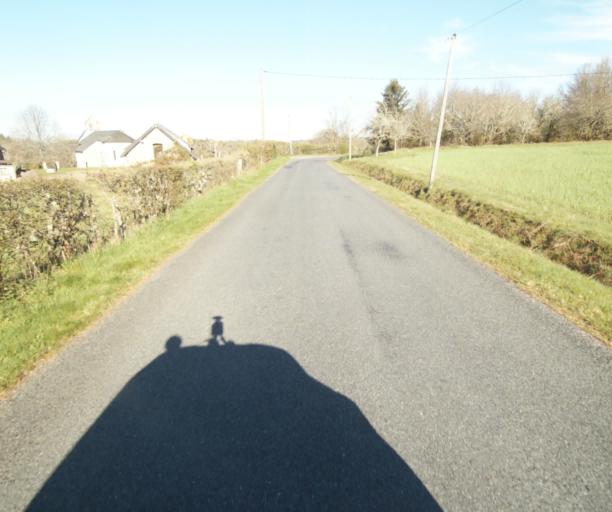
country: FR
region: Limousin
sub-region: Departement de la Correze
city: Correze
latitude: 45.3015
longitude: 1.8693
